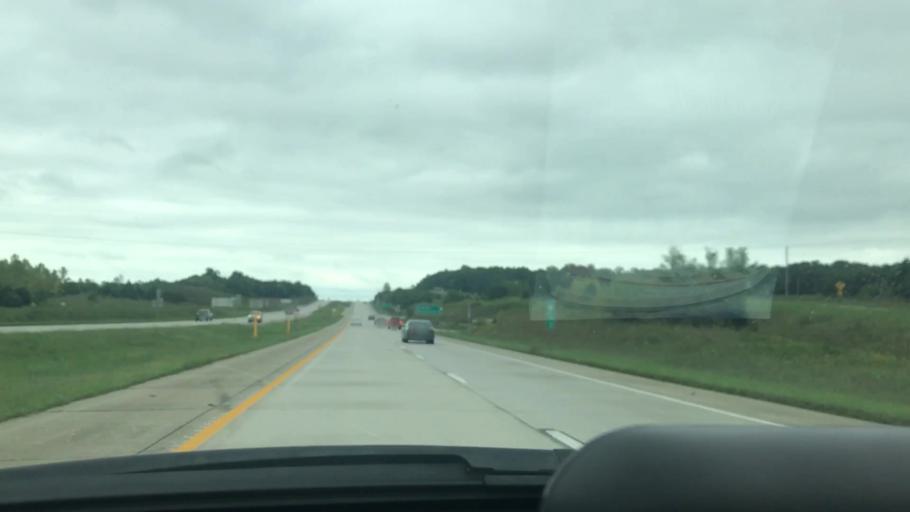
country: US
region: Missouri
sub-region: Greene County
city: Fair Grove
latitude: 37.5146
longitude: -93.1385
